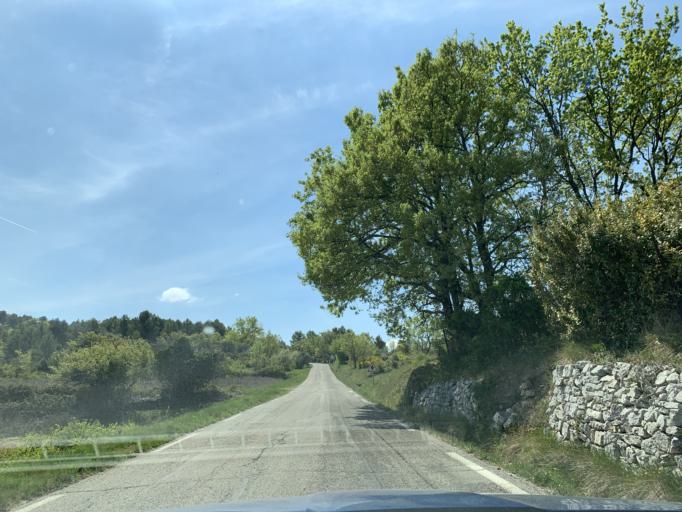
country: FR
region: Provence-Alpes-Cote d'Azur
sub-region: Departement du Vaucluse
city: Saint-Didier
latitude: 43.9976
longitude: 5.1068
